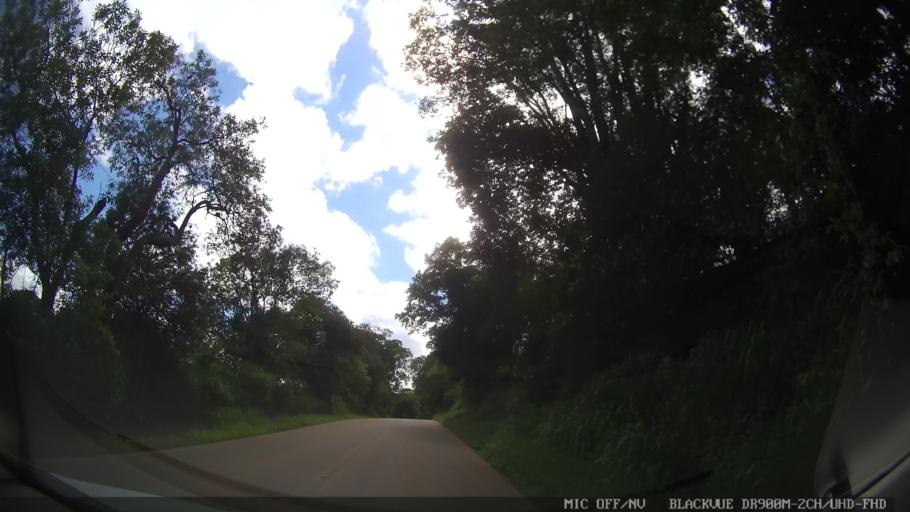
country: BR
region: Sao Paulo
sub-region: Amparo
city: Amparo
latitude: -22.8650
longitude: -46.7343
